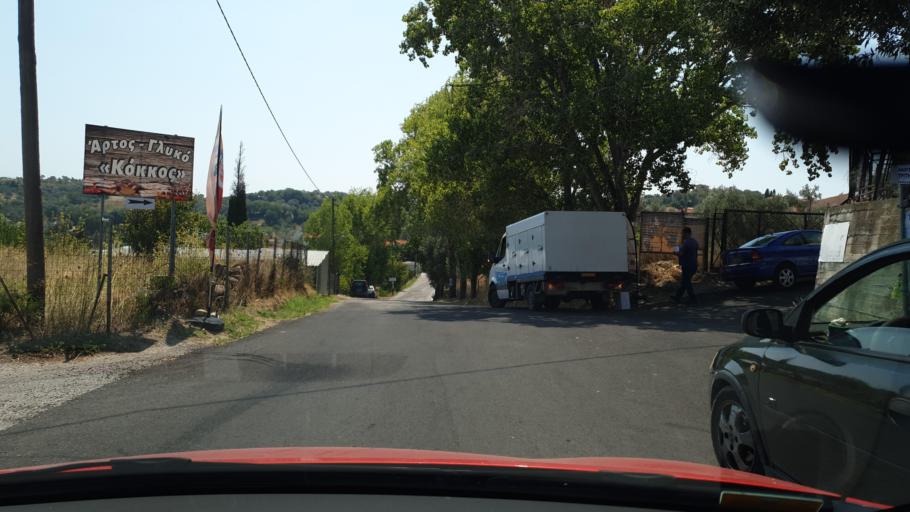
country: GR
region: Central Greece
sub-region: Nomos Evvoias
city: Oxilithos
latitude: 38.5752
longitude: 24.0618
